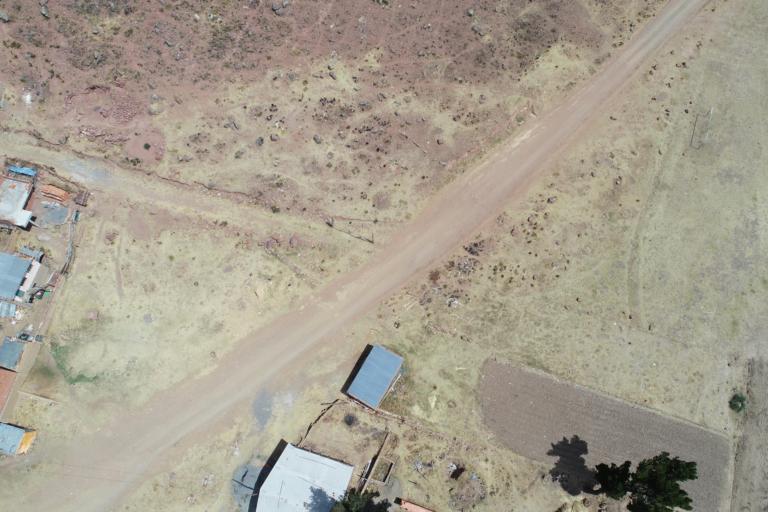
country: BO
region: La Paz
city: Achacachi
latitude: -15.9113
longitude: -68.8848
